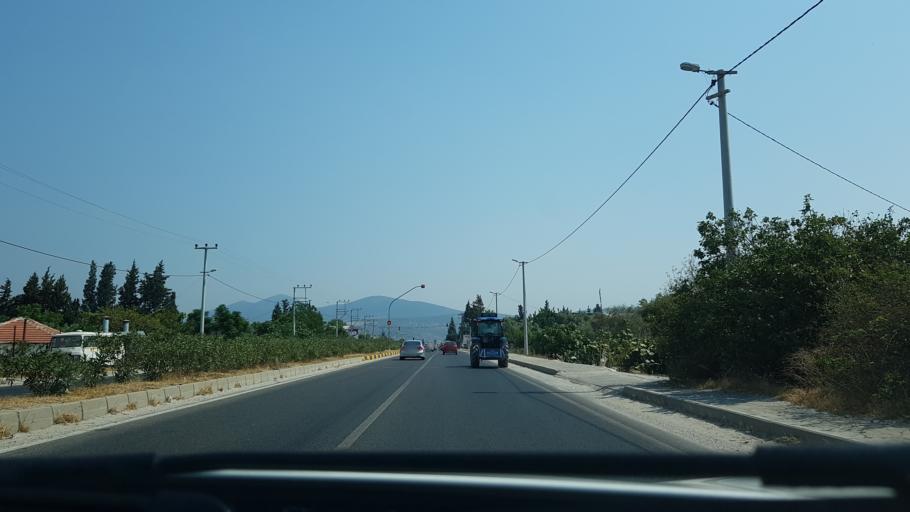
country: TR
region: Mugla
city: Milas
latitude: 37.2395
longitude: 27.7127
